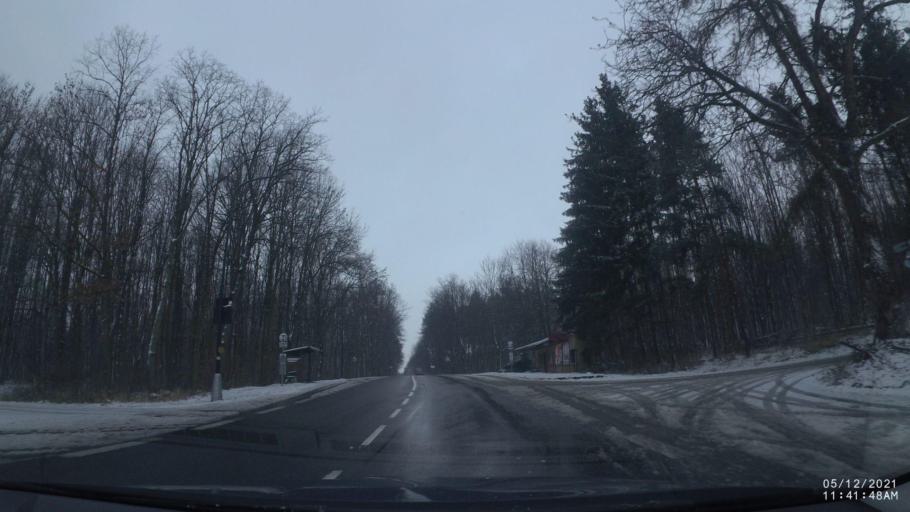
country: CZ
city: Dobruska
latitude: 50.2723
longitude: 16.1941
